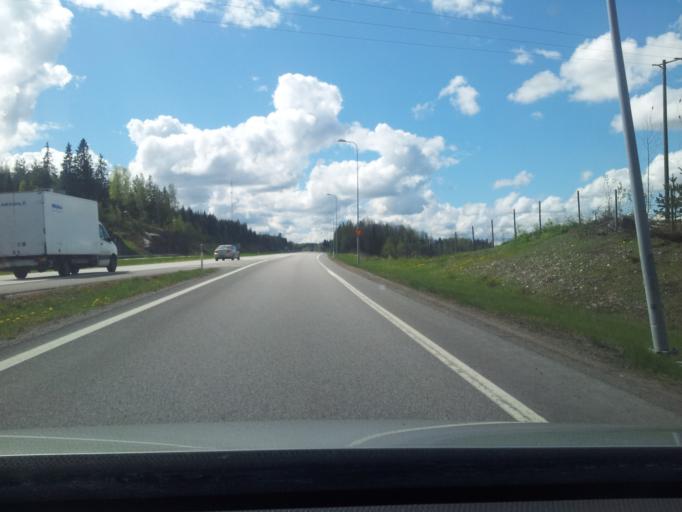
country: FI
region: Uusimaa
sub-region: Loviisa
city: Perna
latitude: 60.4857
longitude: 25.8889
